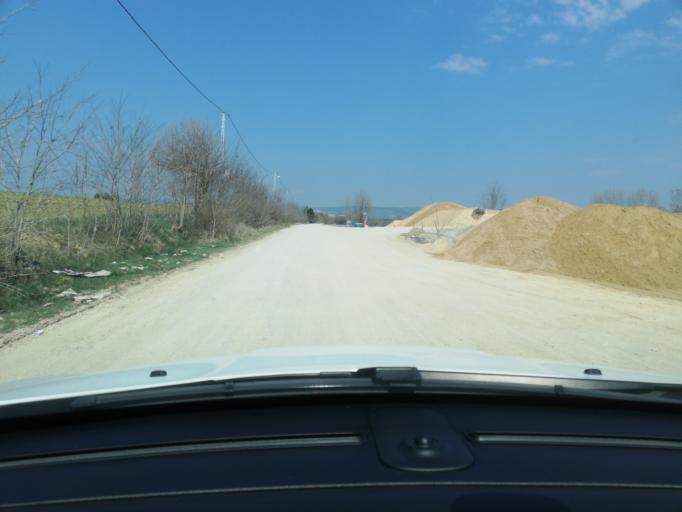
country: TR
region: Kastamonu
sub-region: Cide
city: Kastamonu
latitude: 41.4581
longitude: 33.7675
